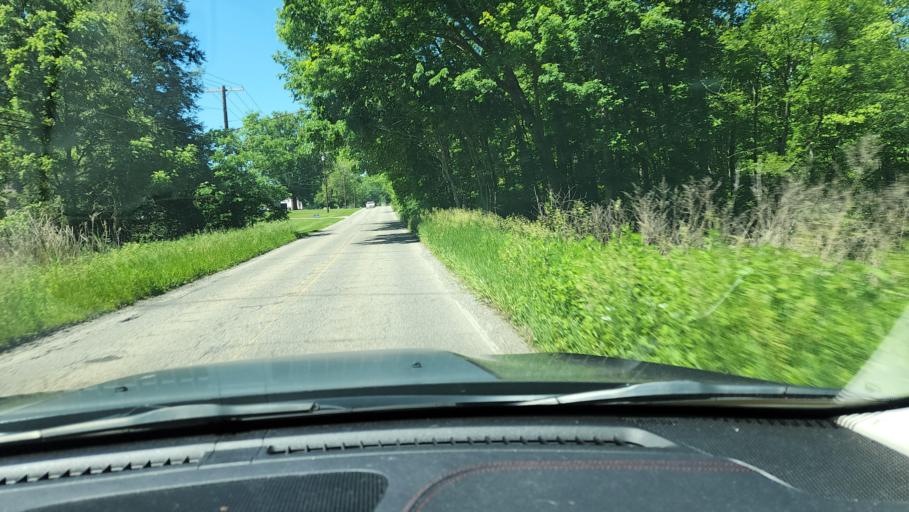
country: US
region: Ohio
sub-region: Trumbull County
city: Niles
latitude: 41.1642
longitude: -80.7785
